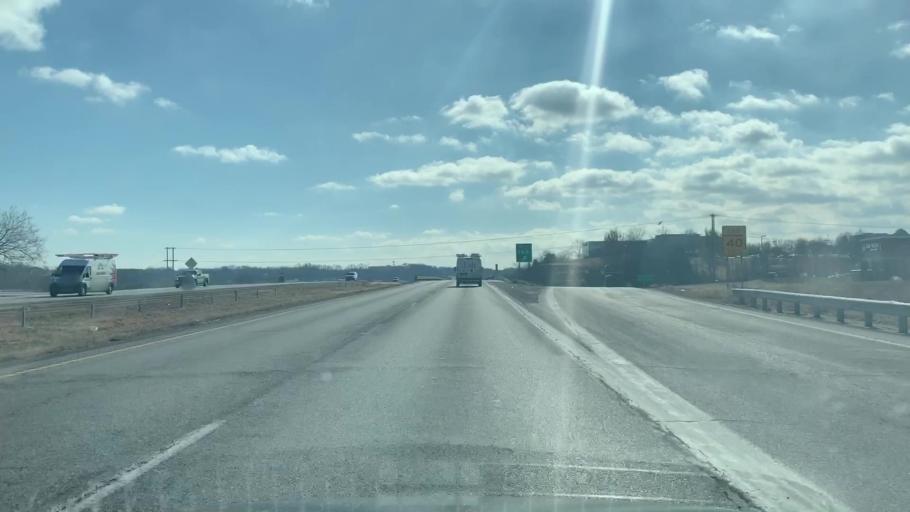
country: US
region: Missouri
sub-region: Jackson County
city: East Independence
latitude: 39.0356
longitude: -94.3619
